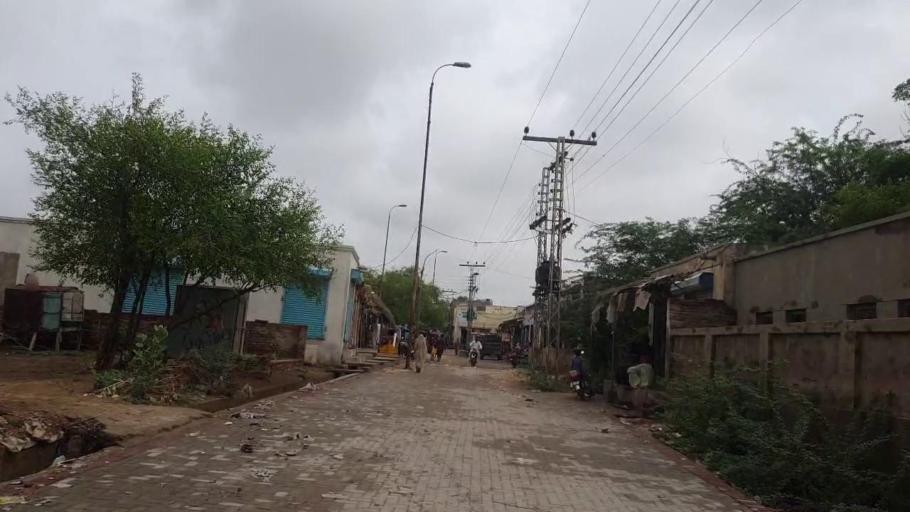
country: PK
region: Sindh
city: Diplo
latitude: 24.4646
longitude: 69.5813
